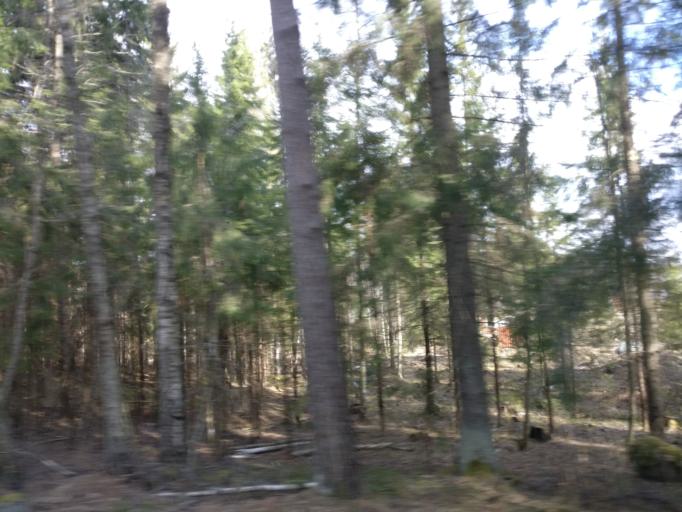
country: FI
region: Varsinais-Suomi
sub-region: Salo
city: Suomusjaervi
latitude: 60.3321
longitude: 23.7042
